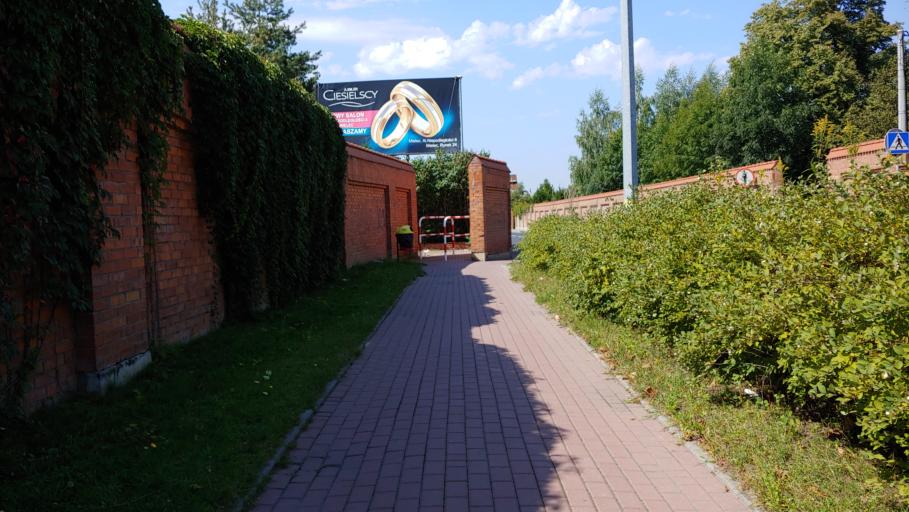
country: PL
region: Subcarpathian Voivodeship
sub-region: Powiat mielecki
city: Mielec
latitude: 50.2883
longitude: 21.4125
